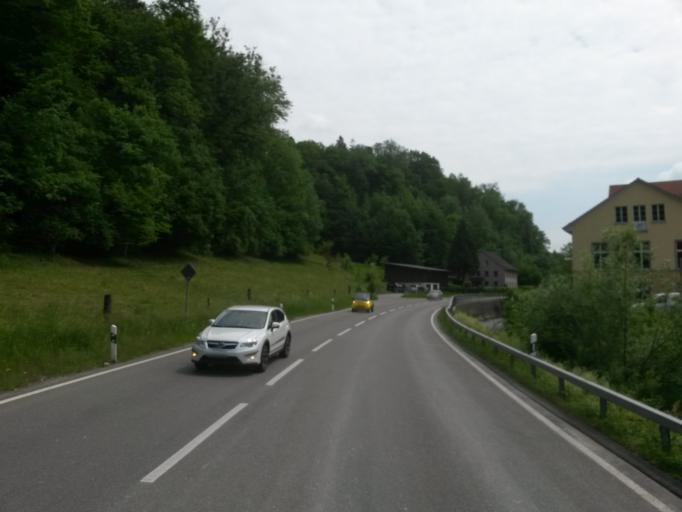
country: CH
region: Zurich
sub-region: Bezirk Pfaeffikon
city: Effretikon / Watt
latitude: 47.4317
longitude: 8.7054
